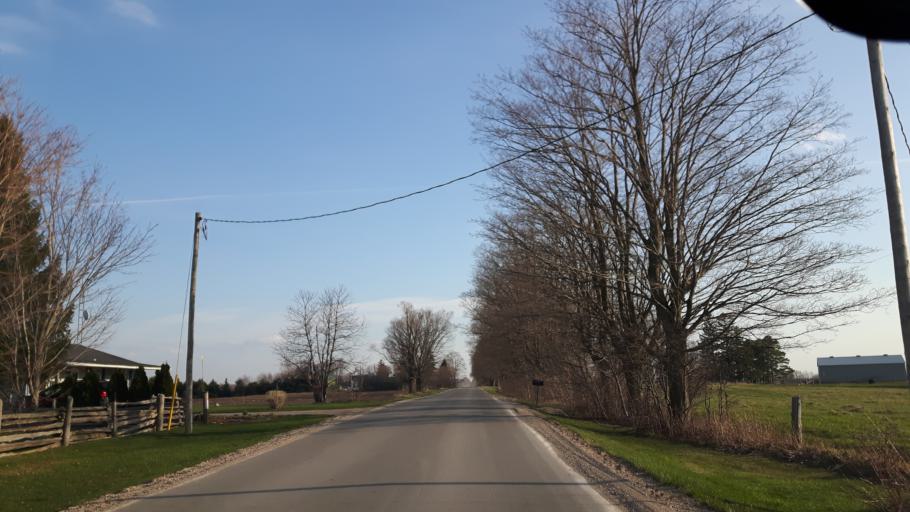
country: CA
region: Ontario
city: Goderich
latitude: 43.6420
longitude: -81.6643
